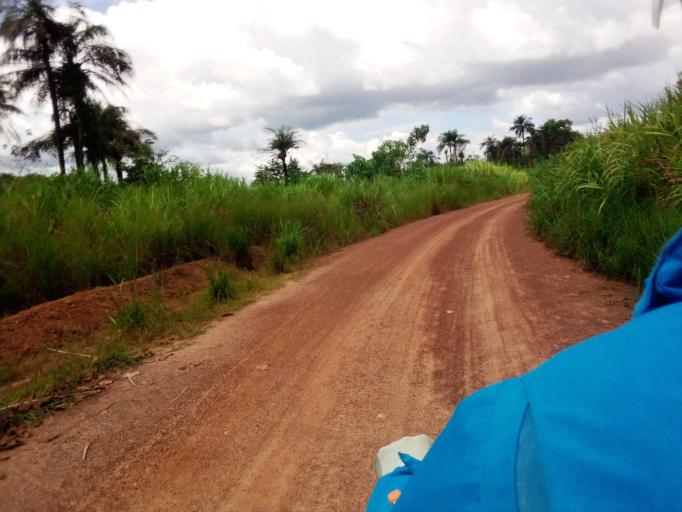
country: SL
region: Eastern Province
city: Simbakoro
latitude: 8.5965
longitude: -10.9850
